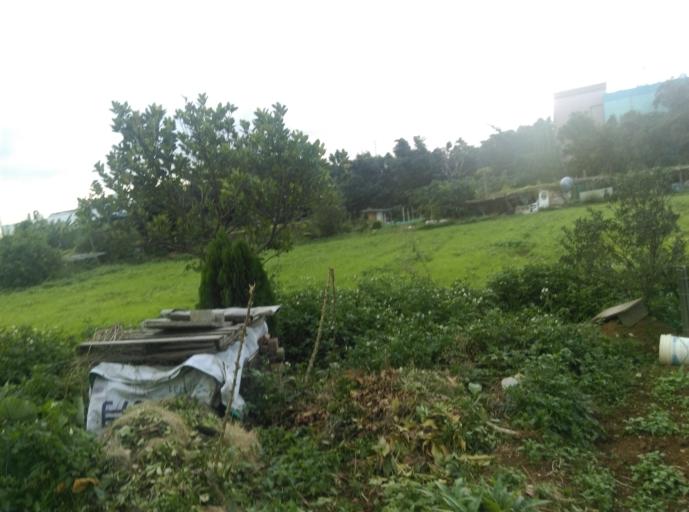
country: TW
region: Taiwan
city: Taoyuan City
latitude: 24.9947
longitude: 121.2513
